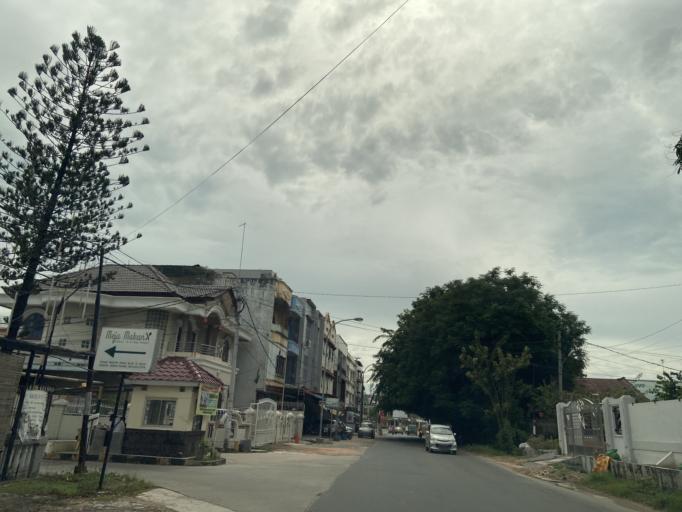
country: SG
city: Singapore
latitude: 1.1411
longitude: 104.0087
